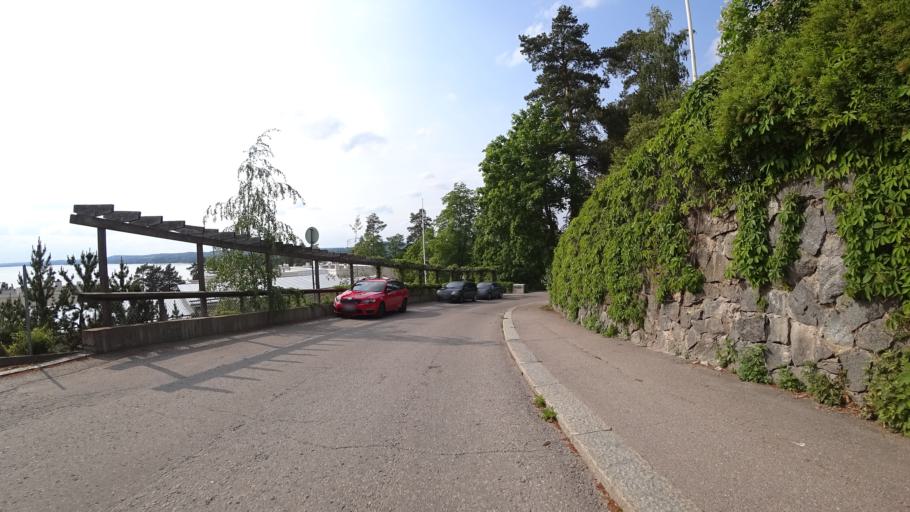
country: FI
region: Pirkanmaa
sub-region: Tampere
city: Tampere
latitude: 61.4953
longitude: 23.7118
